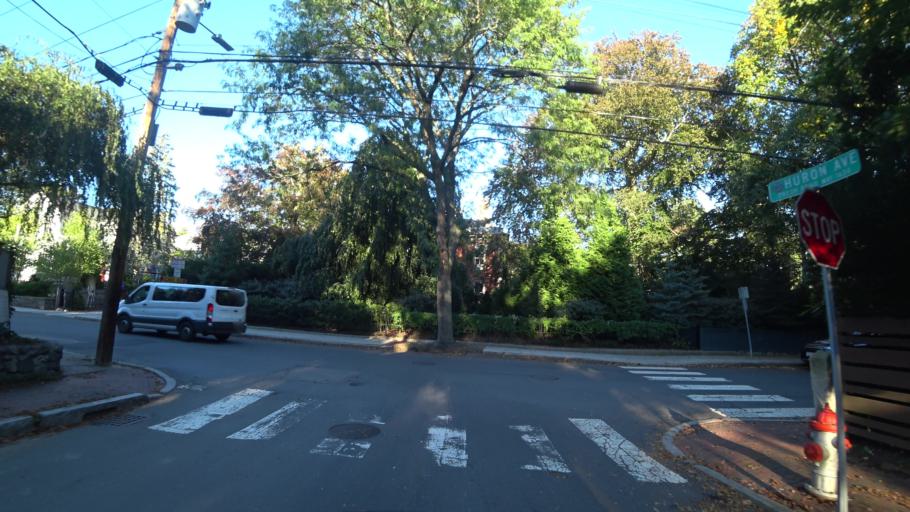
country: US
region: Massachusetts
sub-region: Middlesex County
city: Cambridge
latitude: 42.3853
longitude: -71.1265
